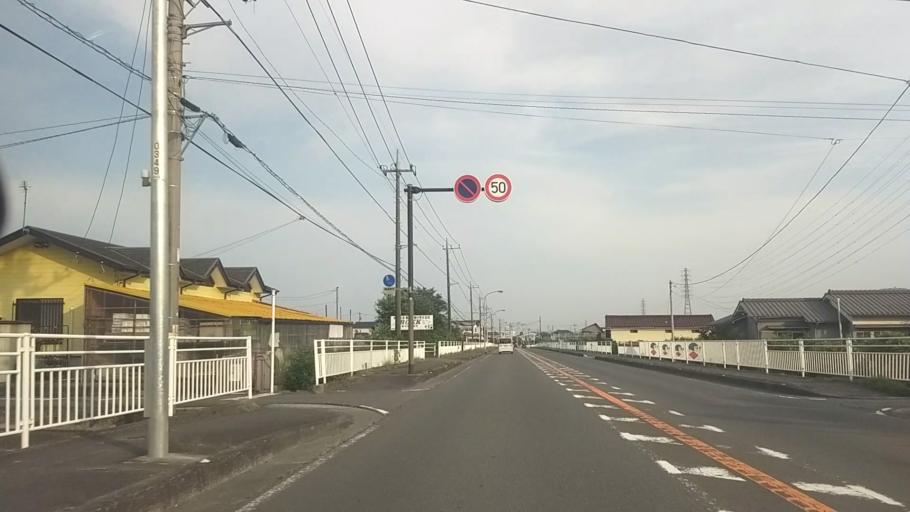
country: JP
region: Kanagawa
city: Odawara
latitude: 35.3395
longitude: 139.1033
